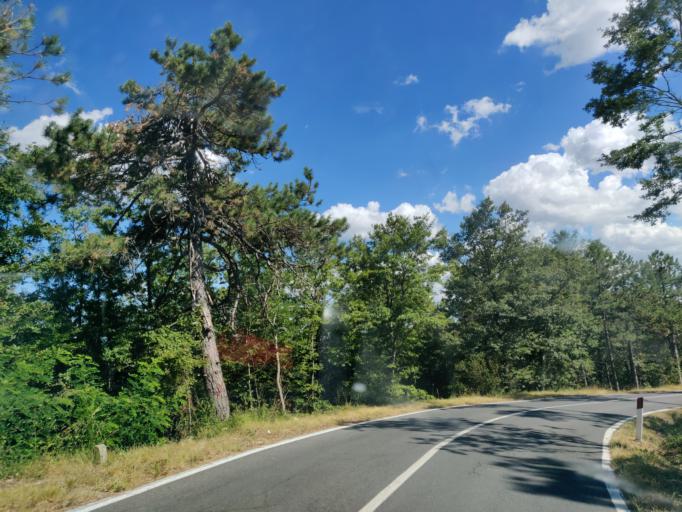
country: IT
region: Tuscany
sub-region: Provincia di Siena
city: Abbadia San Salvatore
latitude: 42.9091
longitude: 11.6931
